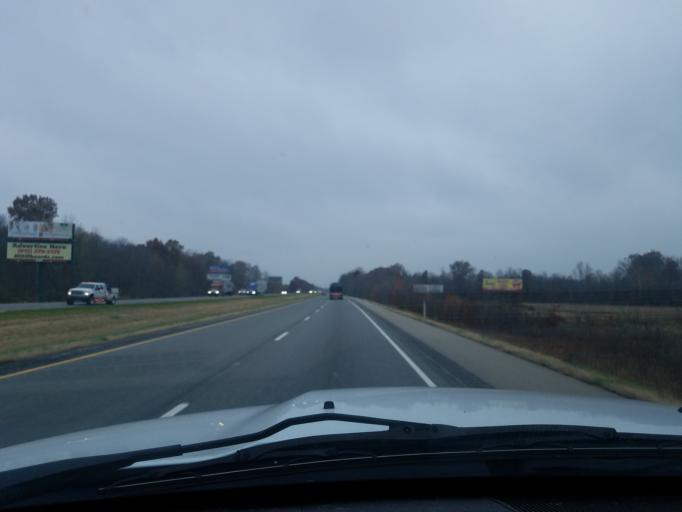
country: US
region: Indiana
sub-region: Scott County
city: Scottsburg
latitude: 38.7146
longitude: -85.7992
